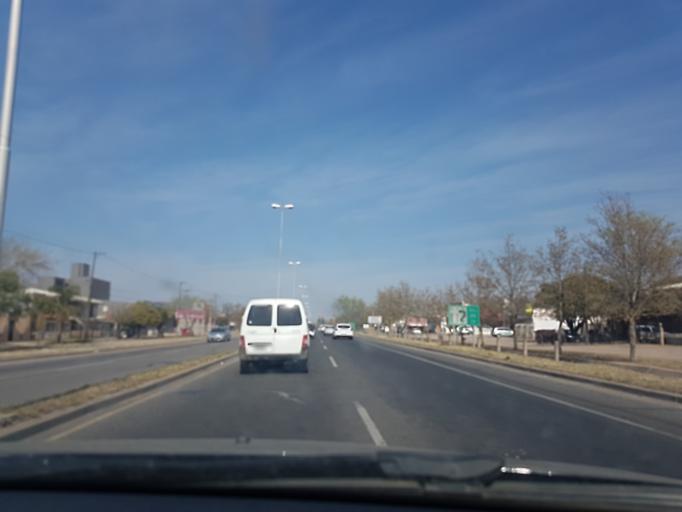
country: AR
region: Cordoba
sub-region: Departamento de Capital
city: Cordoba
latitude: -31.4784
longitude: -64.2380
